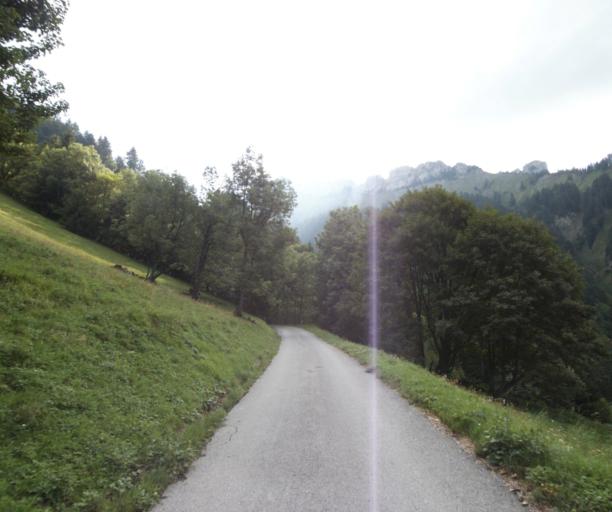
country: CH
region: Vaud
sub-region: Riviera-Pays-d'Enhaut District
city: Caux
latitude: 46.4207
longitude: 6.9833
